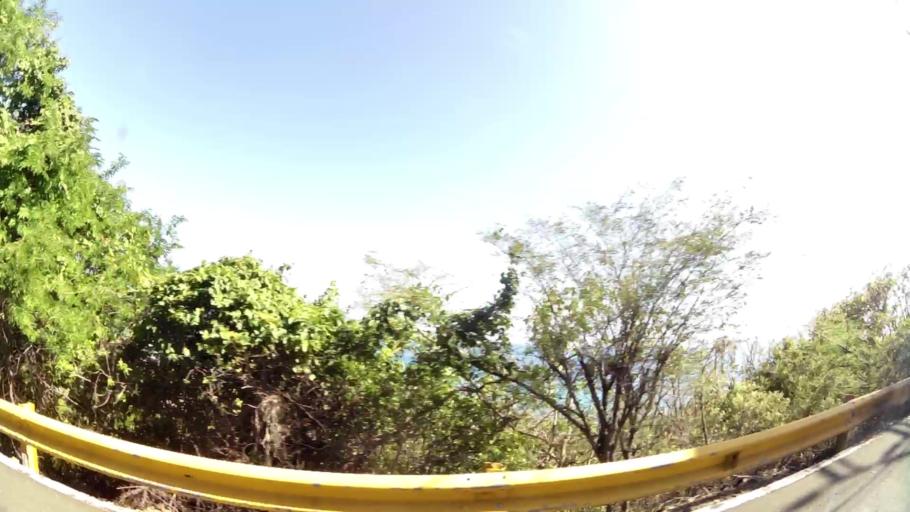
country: VG
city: Tortola
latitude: 18.4131
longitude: -64.5882
